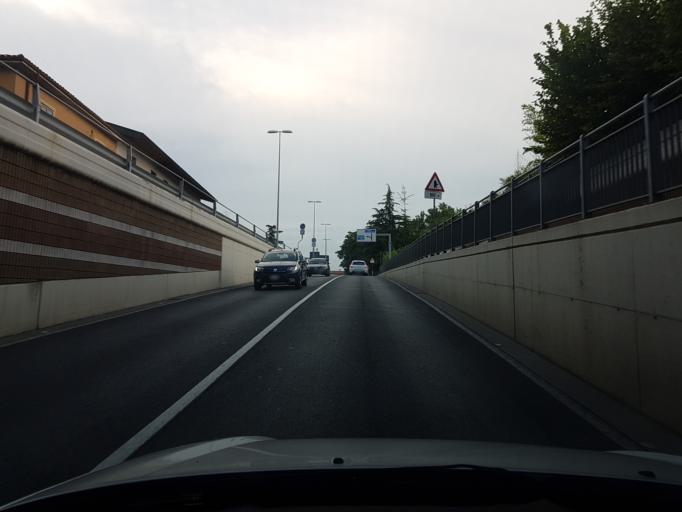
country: IT
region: Friuli Venezia Giulia
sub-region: Provincia di Gorizia
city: Ronchi dei Legionari
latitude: 45.8196
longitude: 13.5139
